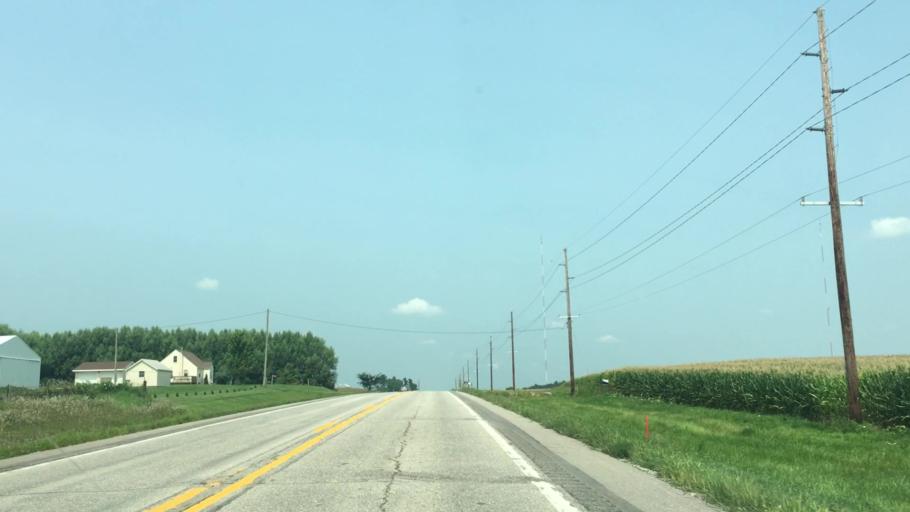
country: US
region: Iowa
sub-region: Benton County
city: Urbana
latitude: 42.2746
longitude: -91.8903
